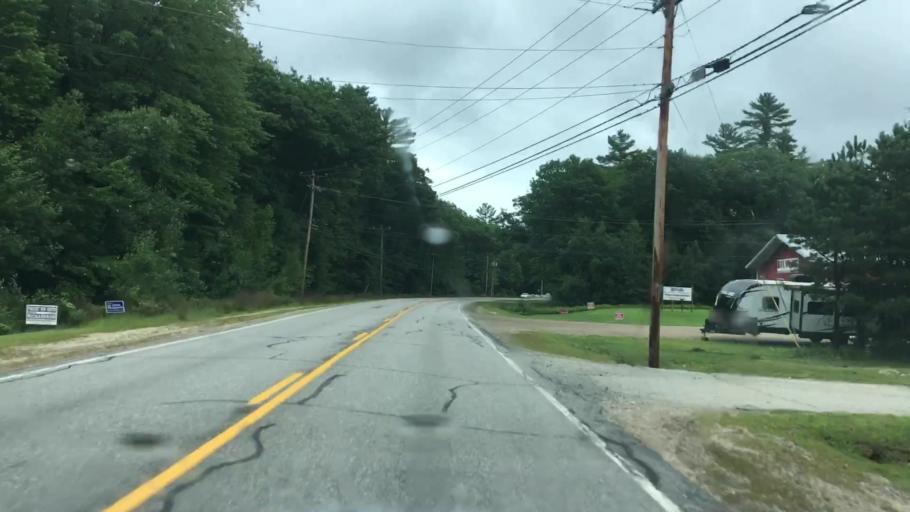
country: US
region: Maine
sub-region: Oxford County
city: Fryeburg
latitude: 44.0104
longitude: -70.9598
